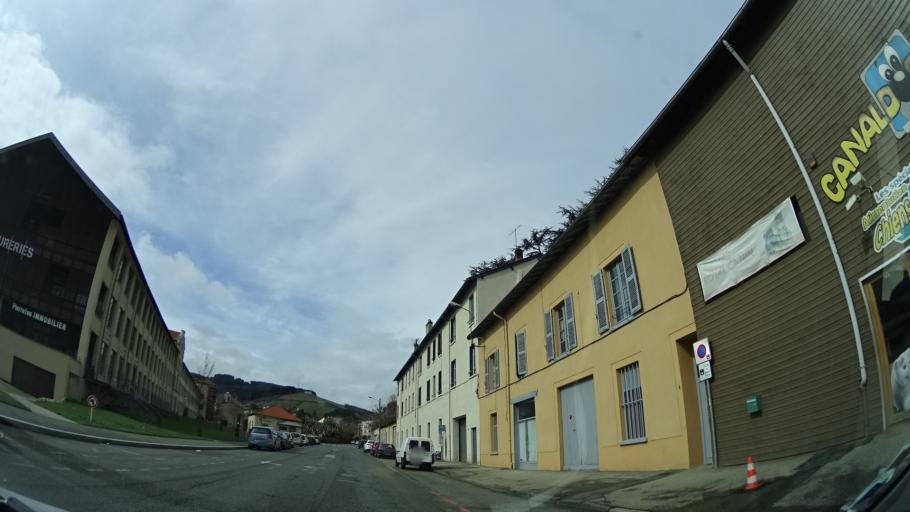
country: FR
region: Rhone-Alpes
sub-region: Departement du Rhone
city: Tarare
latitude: 45.8929
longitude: 4.4409
